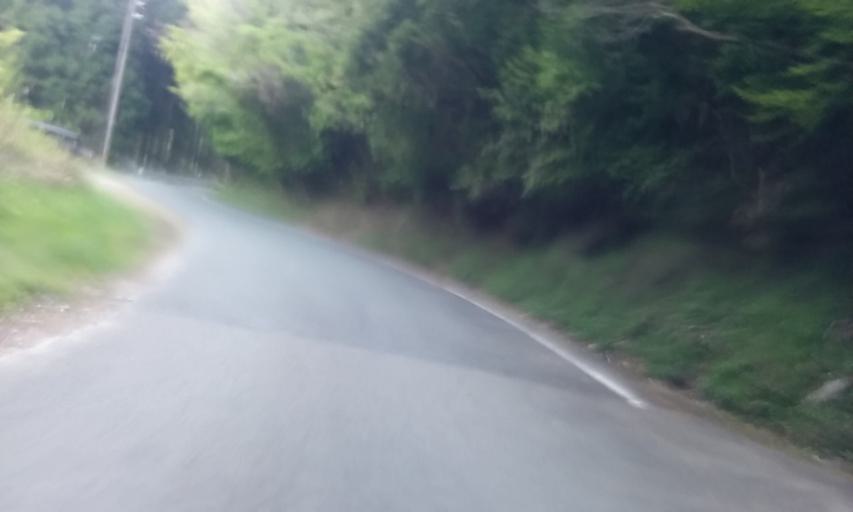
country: JP
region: Ehime
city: Saijo
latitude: 33.7987
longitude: 133.2849
